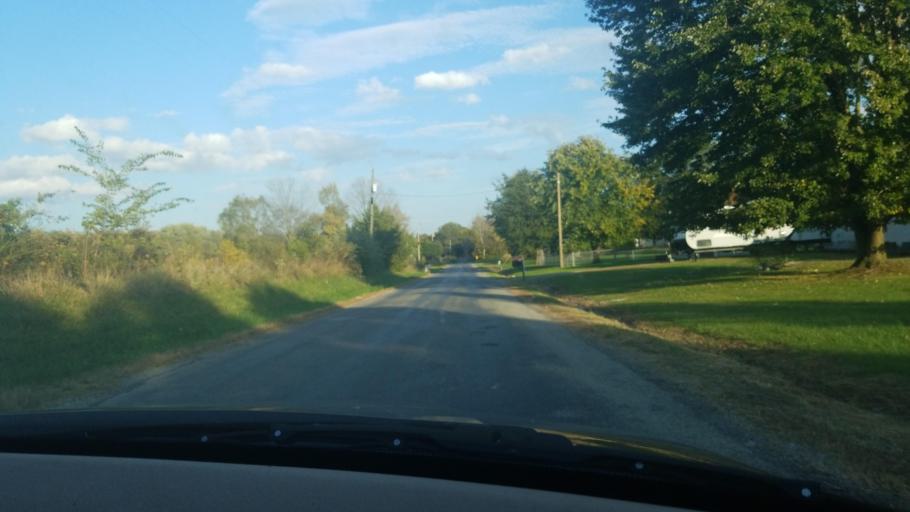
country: US
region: Illinois
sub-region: Williamson County
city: Marion
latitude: 37.7610
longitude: -88.7913
